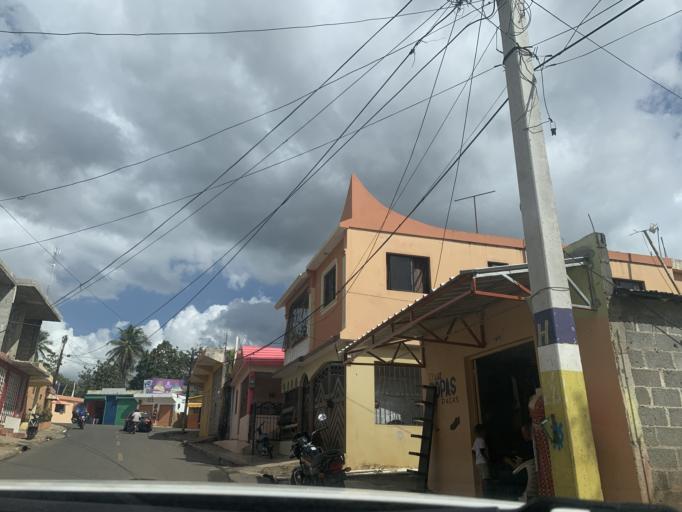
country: DO
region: Monte Plata
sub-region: Yamasa
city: Yamasa
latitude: 18.7737
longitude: -70.0277
